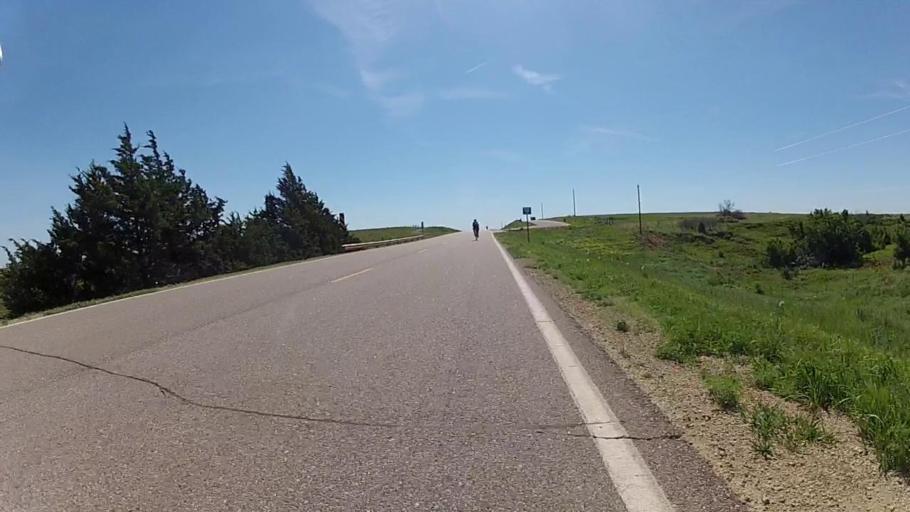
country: US
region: Kansas
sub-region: Barber County
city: Medicine Lodge
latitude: 37.2754
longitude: -98.6977
